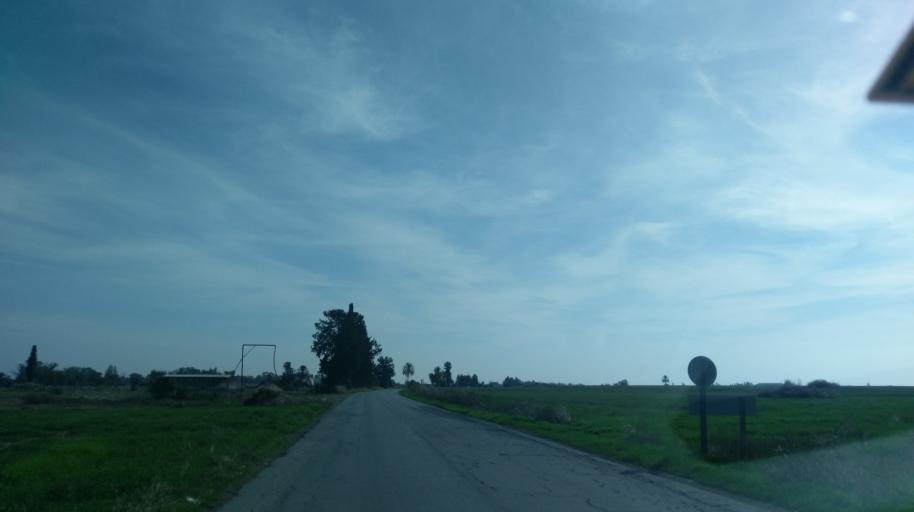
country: CY
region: Larnaka
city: Athienou
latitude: 35.1560
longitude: 33.6219
